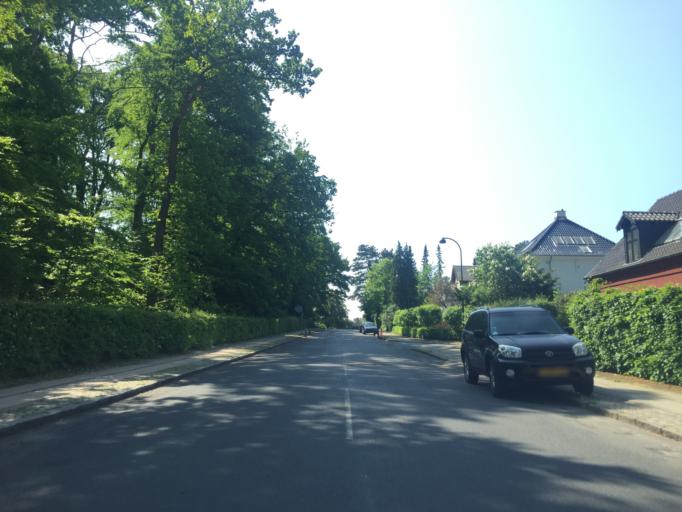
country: DK
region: Capital Region
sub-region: Lyngby-Tarbaek Kommune
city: Kongens Lyngby
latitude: 55.7563
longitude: 12.5441
